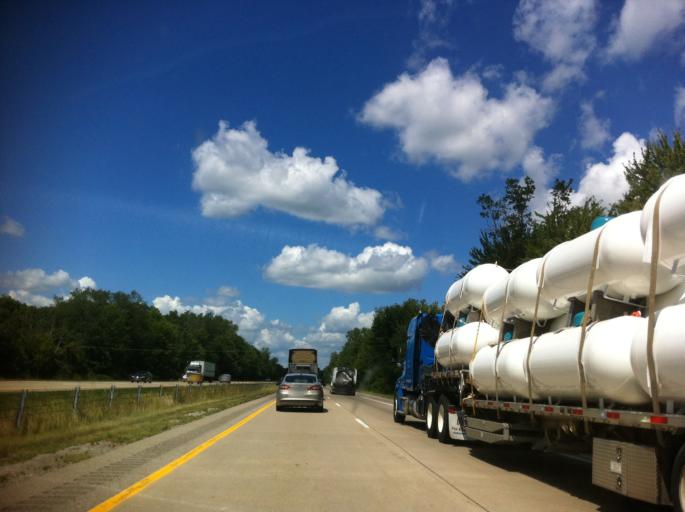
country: US
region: Michigan
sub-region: Monroe County
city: Petersburg
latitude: 41.8789
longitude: -83.6612
